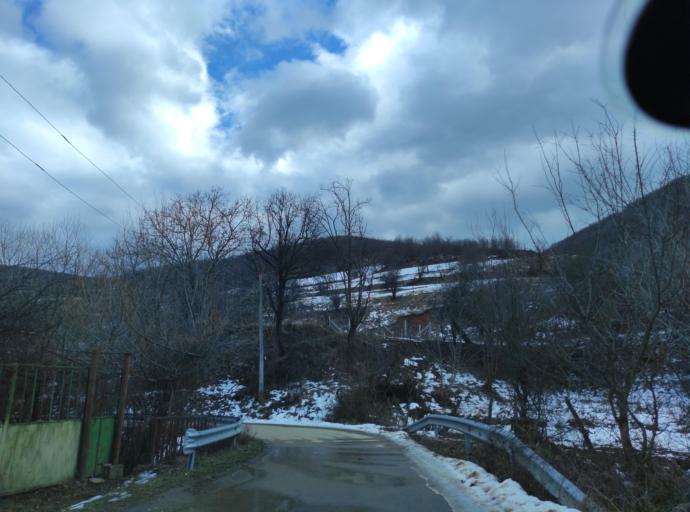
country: BG
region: Montana
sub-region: Obshtina Chiprovtsi
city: Chiprovtsi
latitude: 43.3771
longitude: 22.8732
